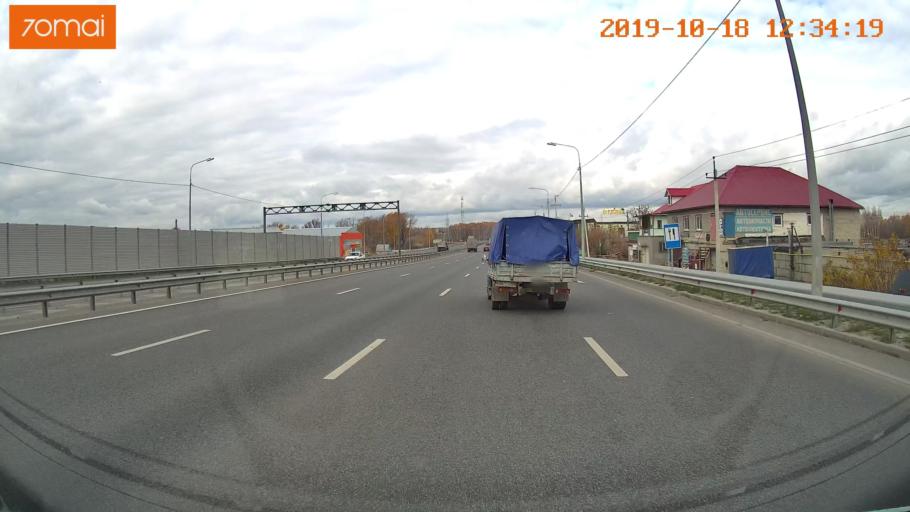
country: RU
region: Rjazan
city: Ryazan'
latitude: 54.6127
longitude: 39.6386
